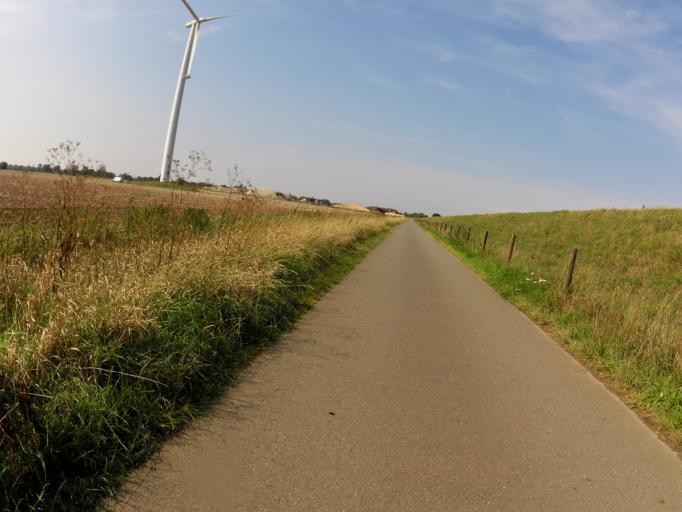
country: DE
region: Lower Saxony
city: Riede
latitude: 53.0021
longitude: 8.9115
